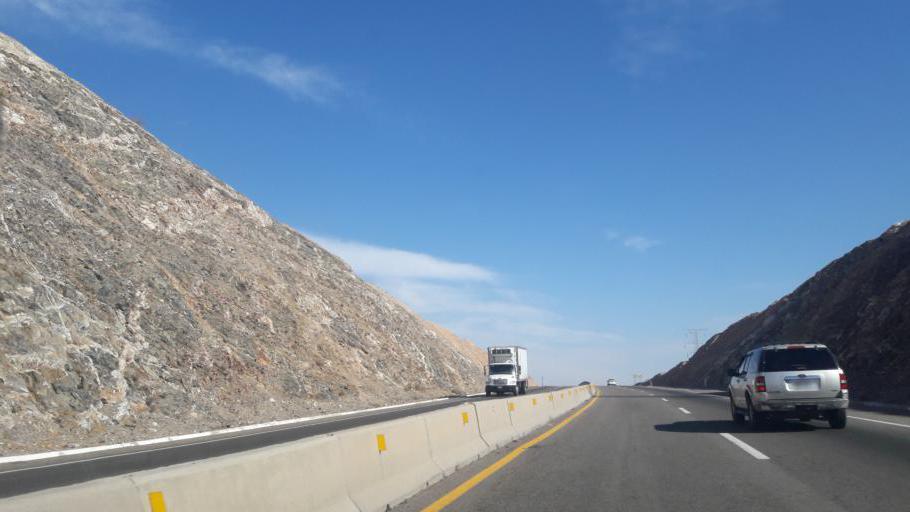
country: MX
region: Baja California
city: Progreso
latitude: 32.5788
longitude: -115.7257
